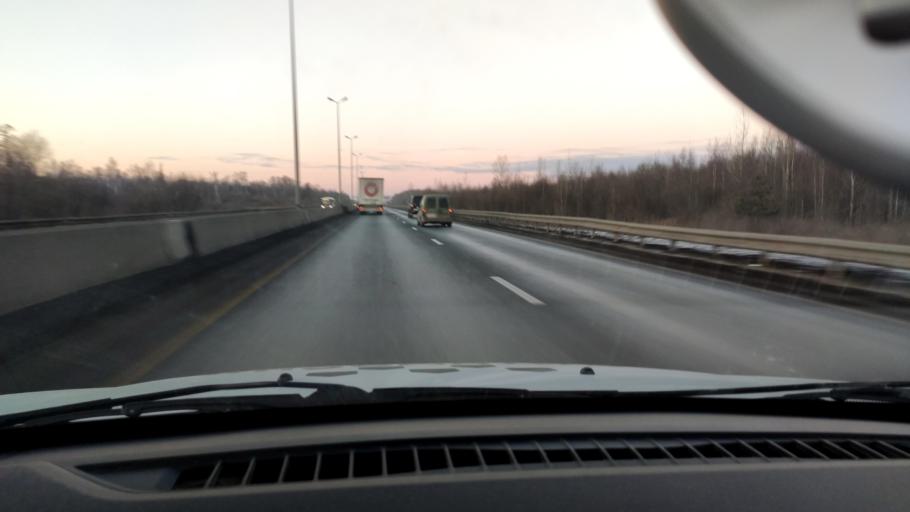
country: RU
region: Perm
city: Kondratovo
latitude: 57.9897
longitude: 56.0656
